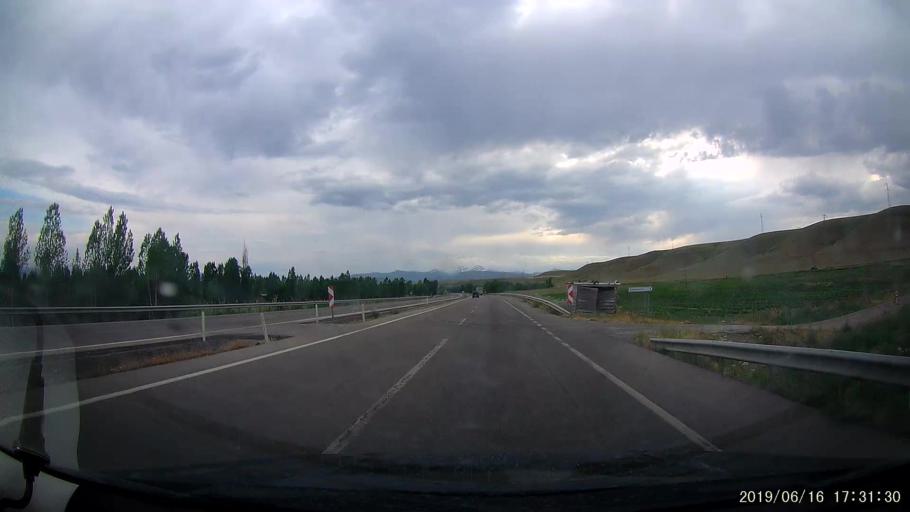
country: TR
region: Erzincan
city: Tercan
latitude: 39.7732
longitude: 40.3215
